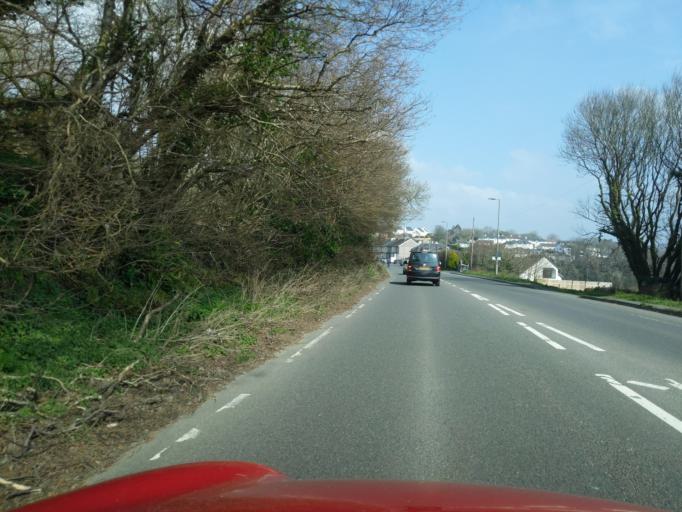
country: GB
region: England
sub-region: Devon
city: Ivybridge
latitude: 50.3956
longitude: -3.8818
